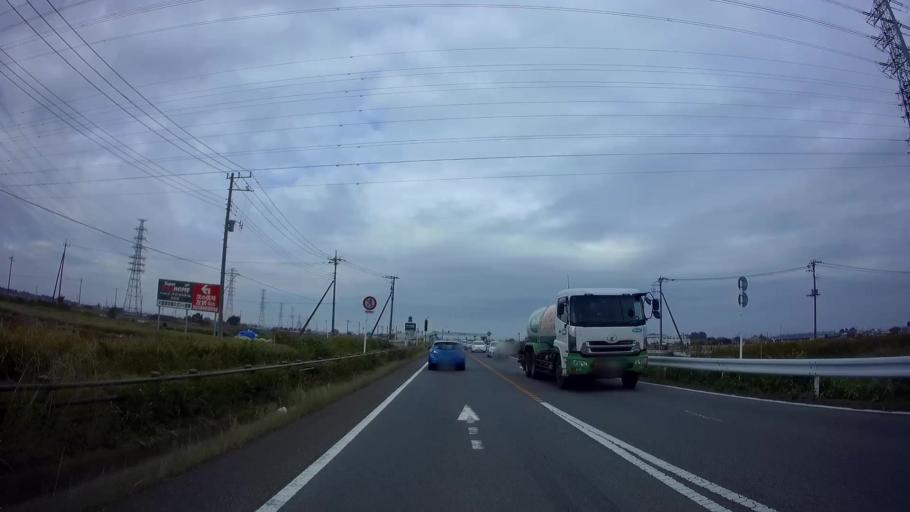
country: JP
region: Saitama
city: Fukayacho
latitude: 36.2038
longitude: 139.3297
